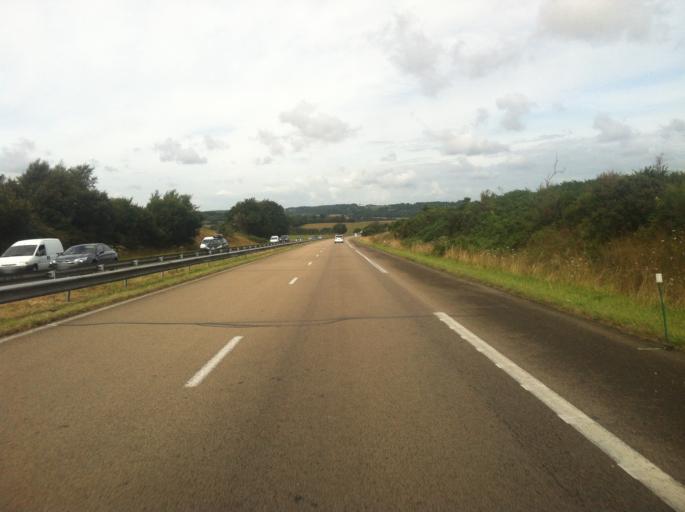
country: FR
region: Brittany
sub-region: Departement du Finistere
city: Guerlesquin
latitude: 48.5709
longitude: -3.6184
